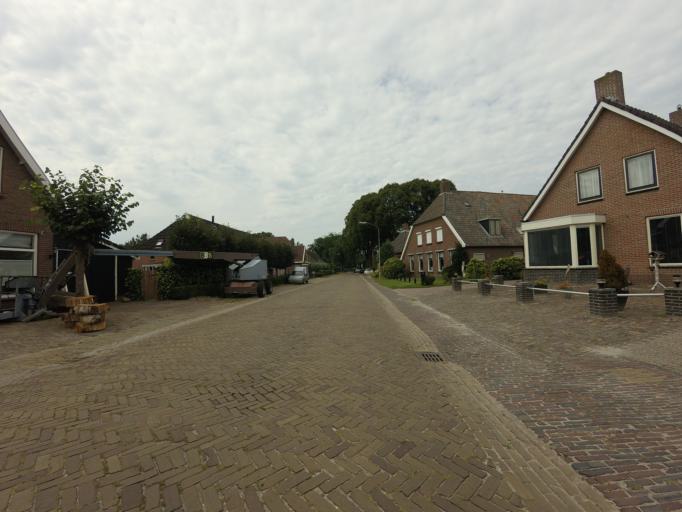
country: NL
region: Drenthe
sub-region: Gemeente Westerveld
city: Dwingeloo
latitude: 52.8322
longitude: 6.3707
